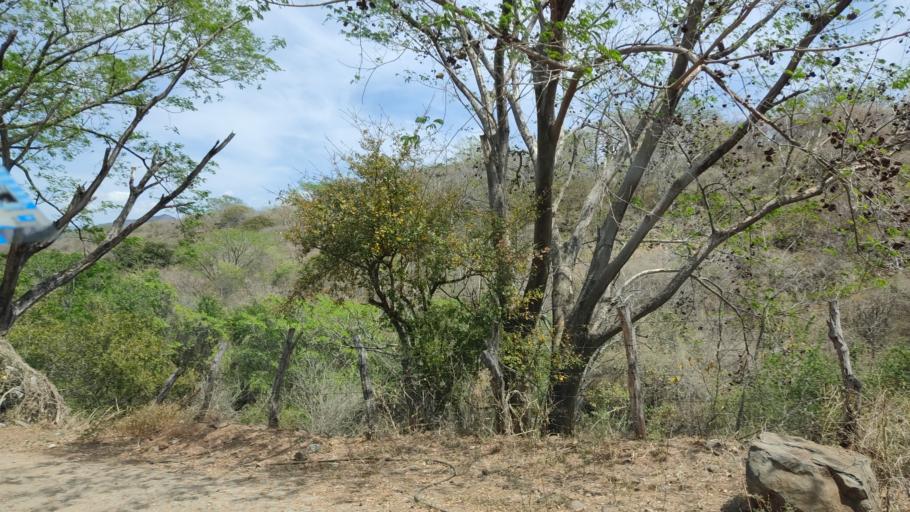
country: MX
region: Nayarit
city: Santa Maria del Oro
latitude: 21.5143
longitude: -104.5882
